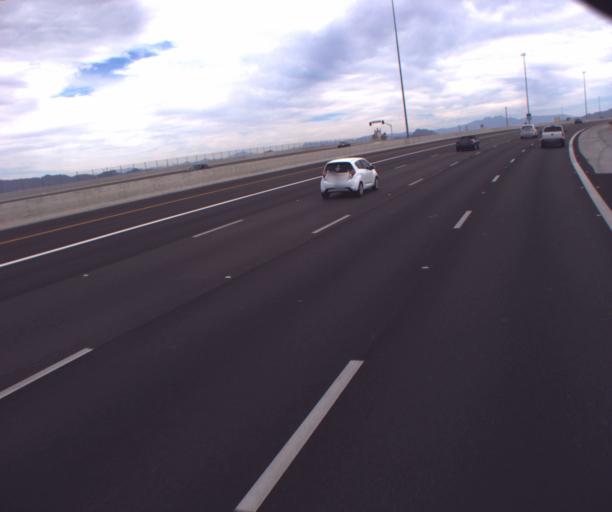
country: US
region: Arizona
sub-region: Maricopa County
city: Mesa
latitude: 33.4441
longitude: -111.8612
